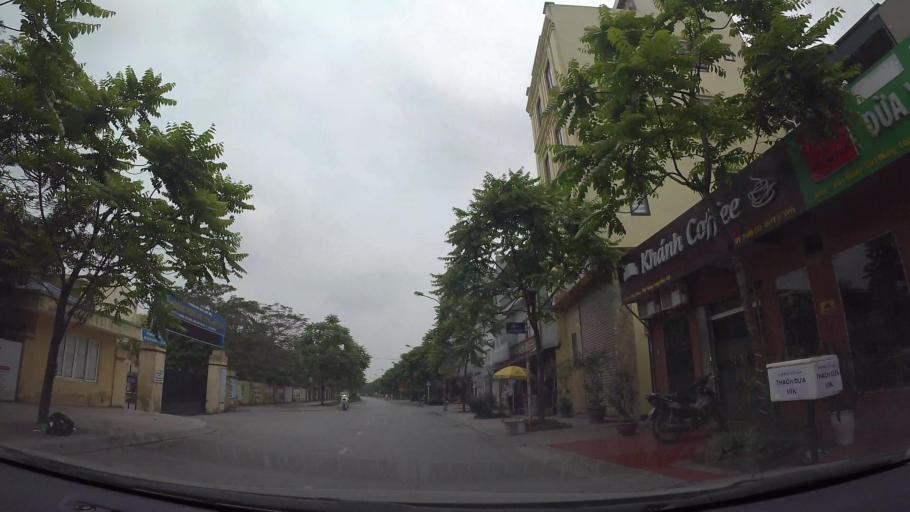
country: VN
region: Ha Noi
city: Trau Quy
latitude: 21.0606
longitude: 105.9006
